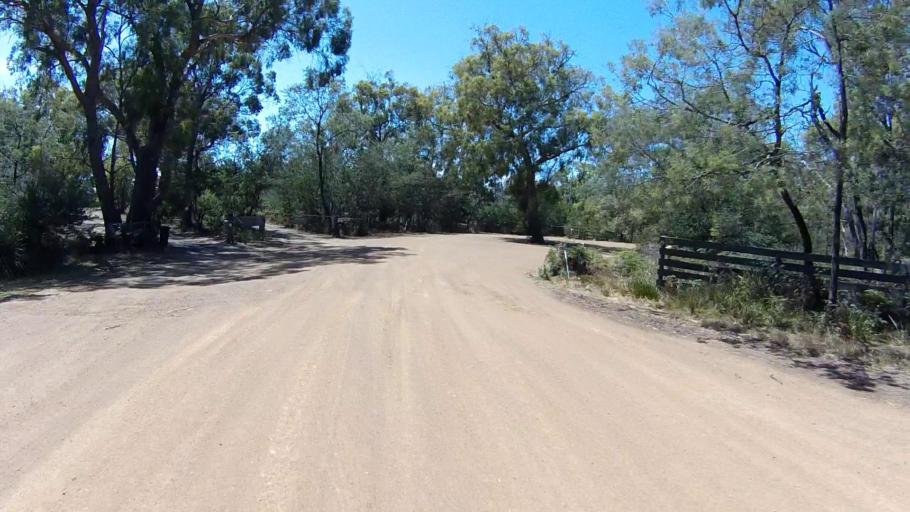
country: AU
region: Tasmania
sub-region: Clarence
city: Sandford
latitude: -42.9320
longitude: 147.5180
